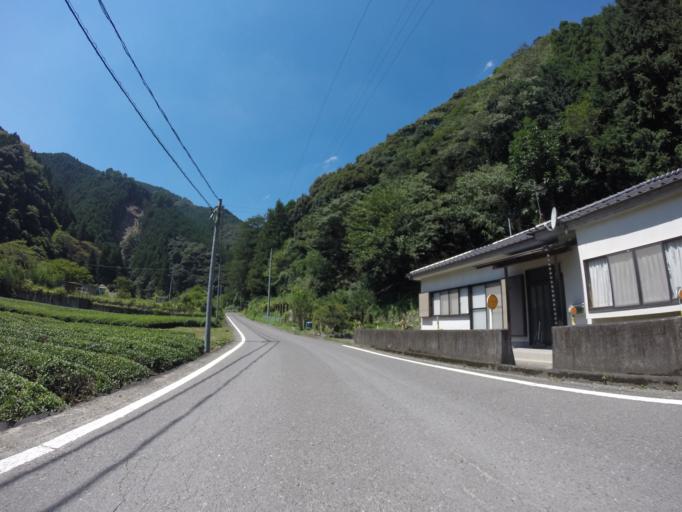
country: JP
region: Shizuoka
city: Shizuoka-shi
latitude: 35.0546
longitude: 138.2404
